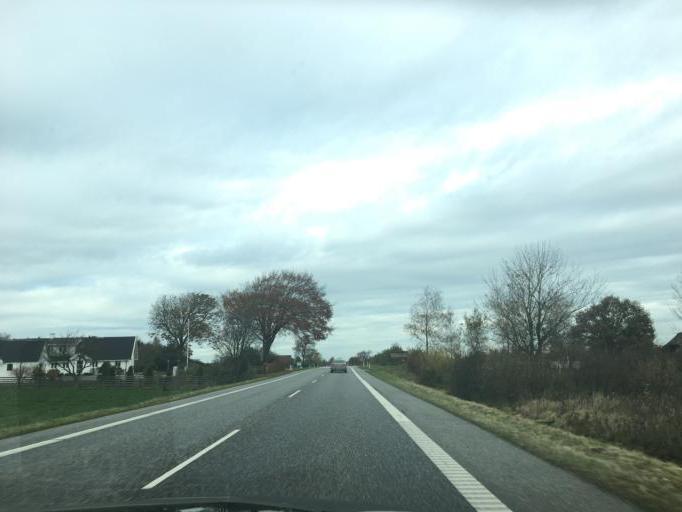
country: DK
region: South Denmark
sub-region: Vejle Kommune
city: Vejle
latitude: 55.6364
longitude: 9.4956
